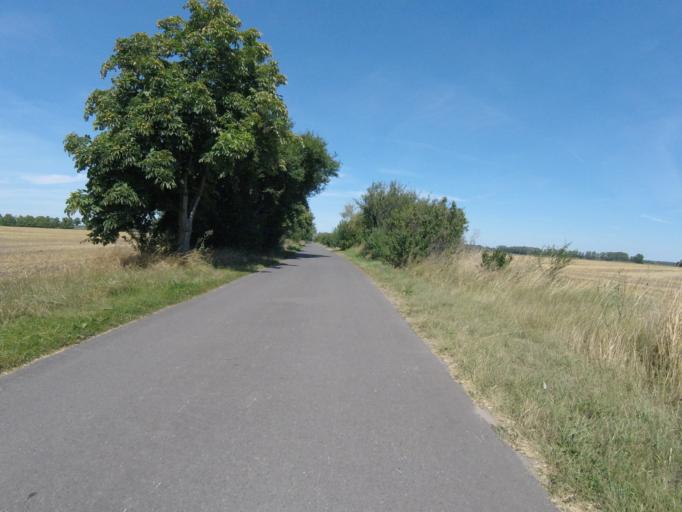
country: DE
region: Brandenburg
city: Mittenwalde
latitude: 52.2782
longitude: 13.5429
